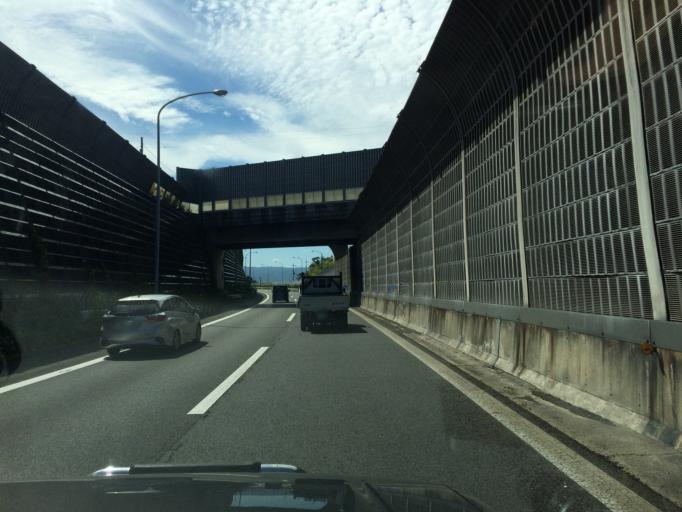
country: JP
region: Osaka
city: Izumi
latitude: 34.4783
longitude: 135.4635
